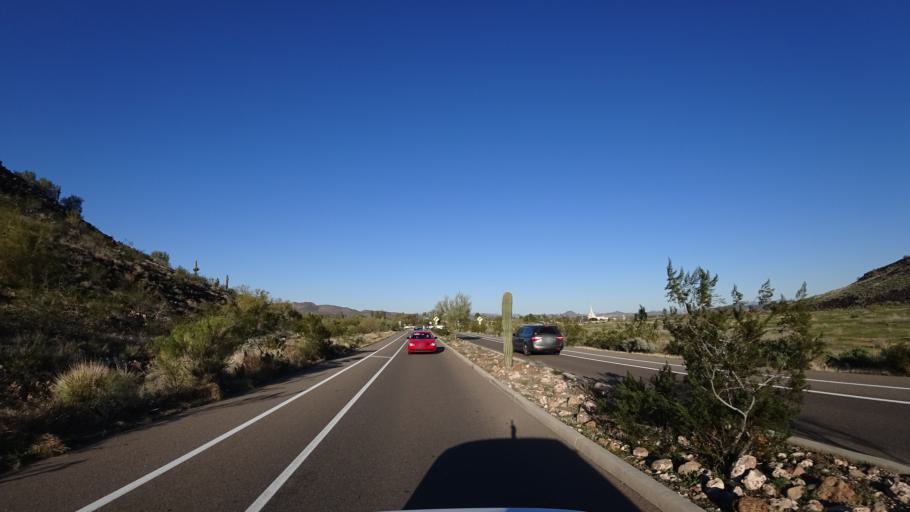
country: US
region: Arizona
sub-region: Maricopa County
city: Peoria
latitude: 33.6963
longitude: -112.1806
